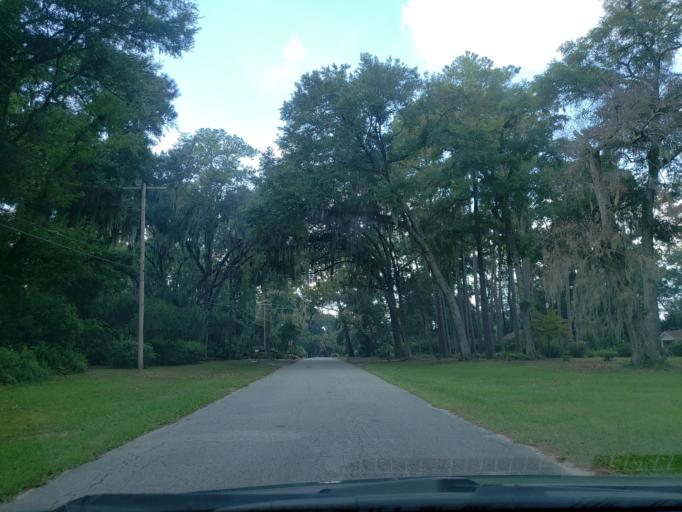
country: US
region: Georgia
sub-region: Chatham County
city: Montgomery
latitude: 31.9295
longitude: -81.0981
